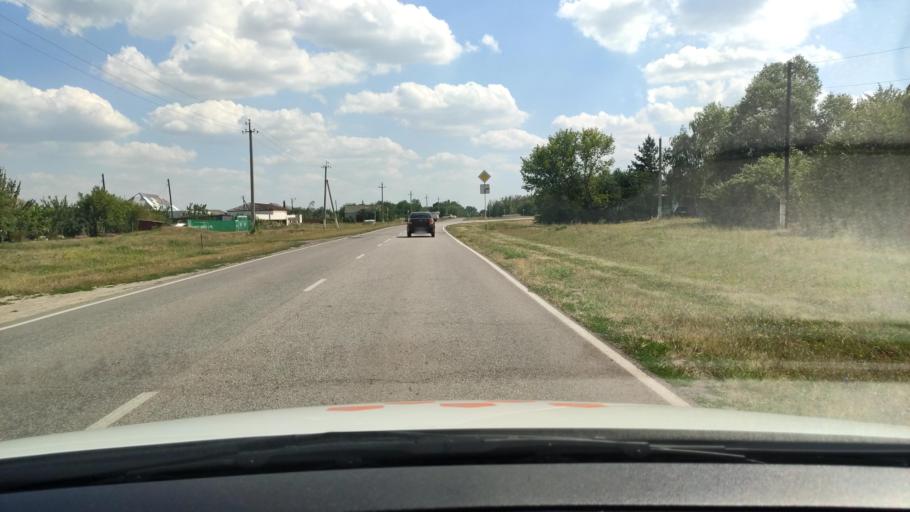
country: RU
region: Voronezj
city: Verkhnyaya Khava
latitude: 51.6826
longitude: 39.9391
